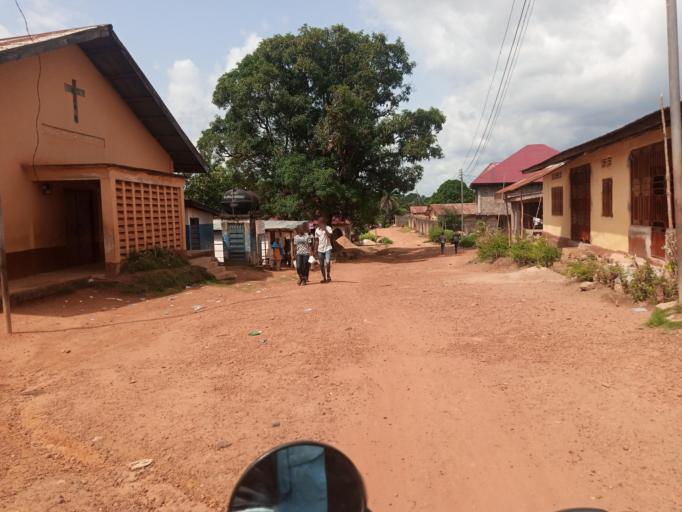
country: SL
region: Southern Province
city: Bo
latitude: 7.9765
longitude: -11.7330
